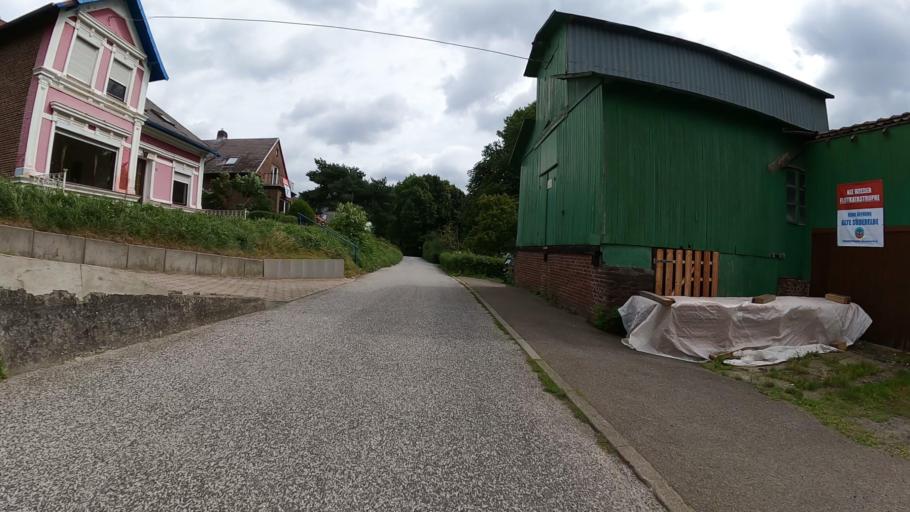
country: DE
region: Hamburg
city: Altona
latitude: 53.5202
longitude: 9.8655
